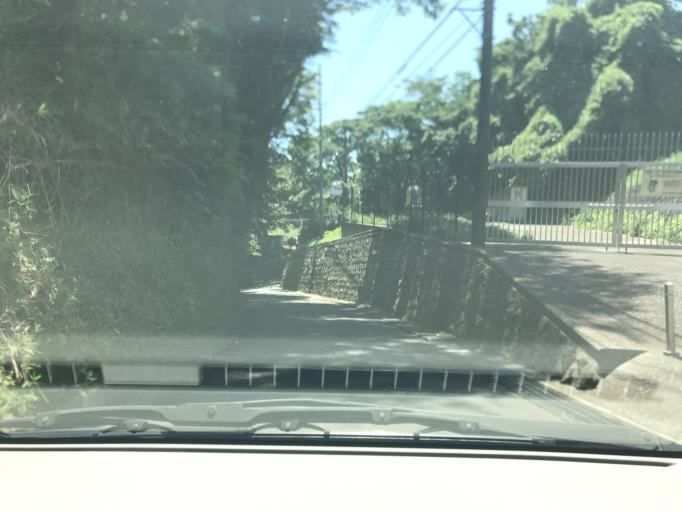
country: JP
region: Kanagawa
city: Fujisawa
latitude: 35.3497
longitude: 139.4411
